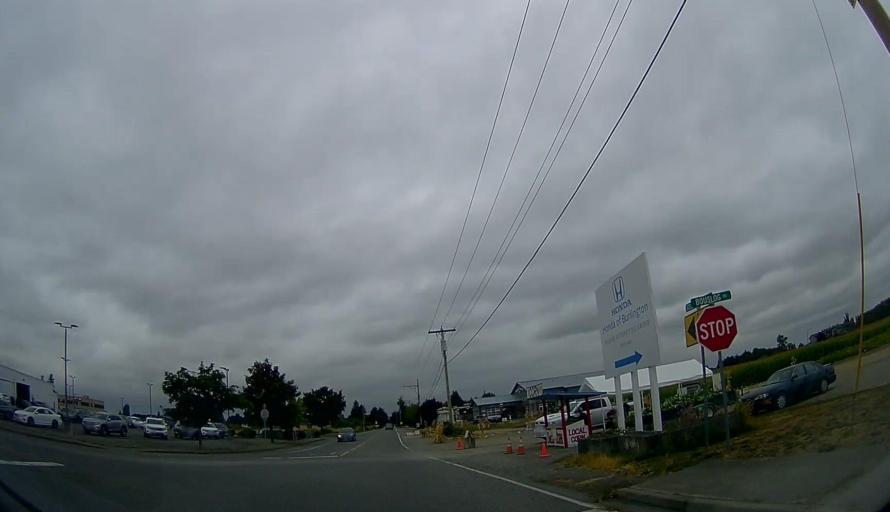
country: US
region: Washington
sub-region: Skagit County
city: Burlington
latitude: 48.4540
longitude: -122.3451
